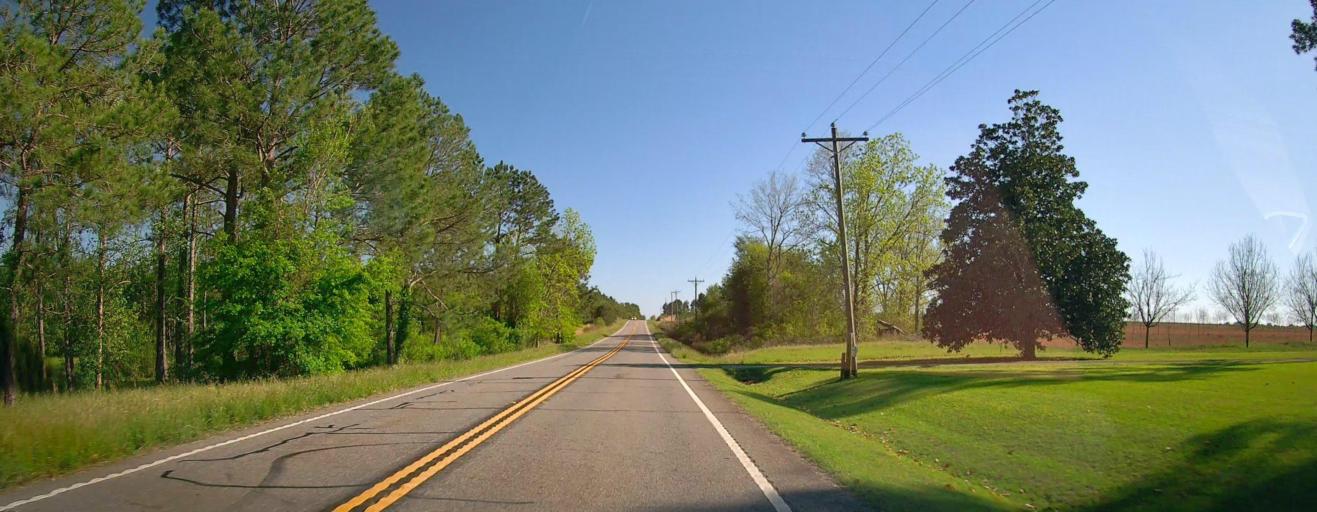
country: US
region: Georgia
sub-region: Wilcox County
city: Rochelle
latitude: 31.8384
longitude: -83.4890
